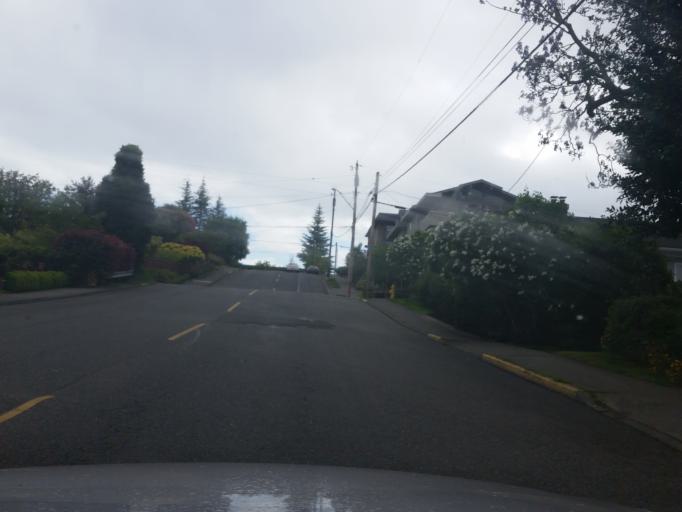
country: US
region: Washington
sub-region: Snohomish County
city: Edmonds
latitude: 47.8118
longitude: -122.3723
